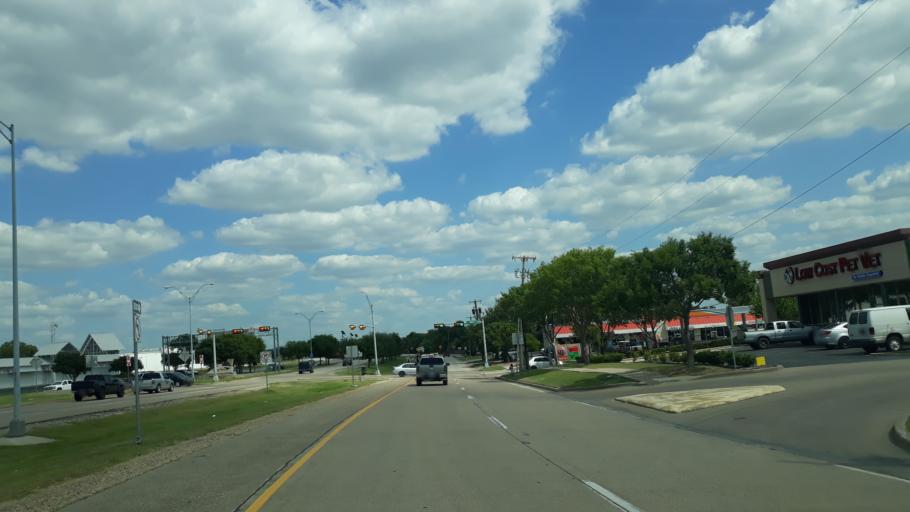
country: US
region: Texas
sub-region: Dallas County
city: Irving
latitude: 32.8344
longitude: -96.9893
